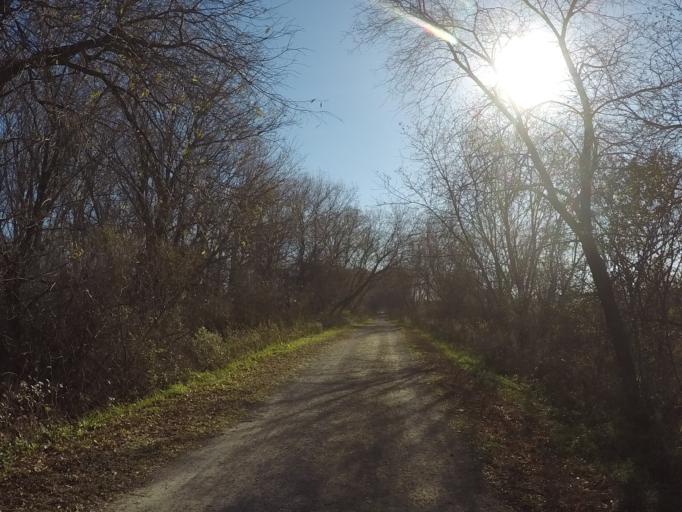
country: US
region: Wisconsin
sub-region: Dane County
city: Deerfield
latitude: 43.0502
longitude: -89.0626
